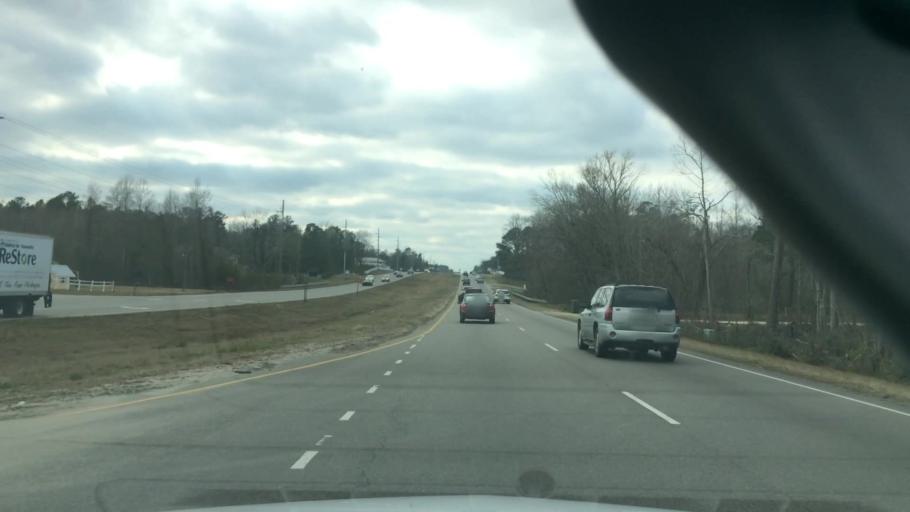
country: US
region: North Carolina
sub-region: Brunswick County
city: Shallotte
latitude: 34.0127
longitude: -78.2863
